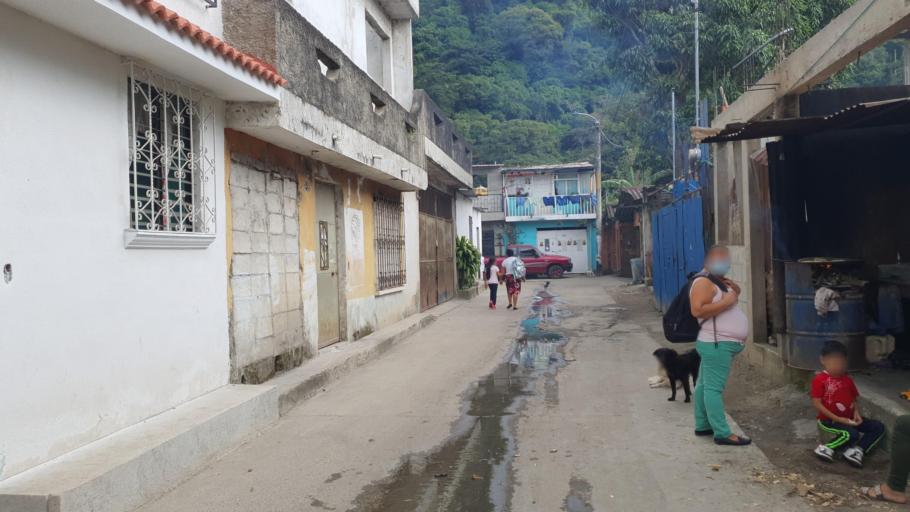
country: GT
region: Guatemala
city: Villa Canales
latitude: 14.4646
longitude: -90.5308
